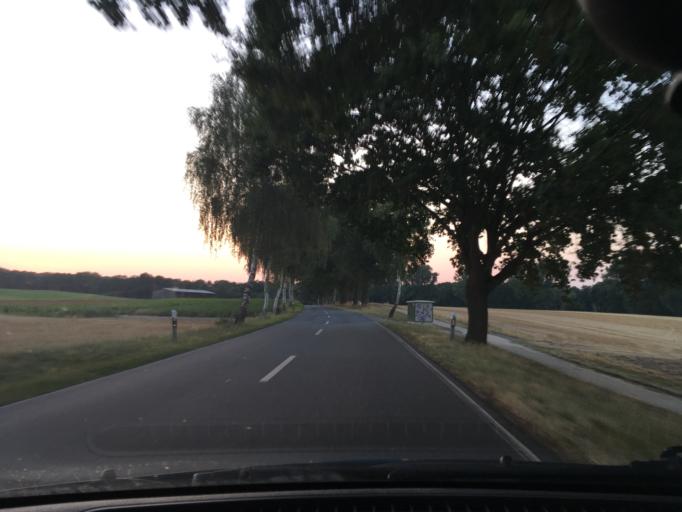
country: DE
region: Lower Saxony
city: Barnstedt
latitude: 53.1533
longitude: 10.3511
